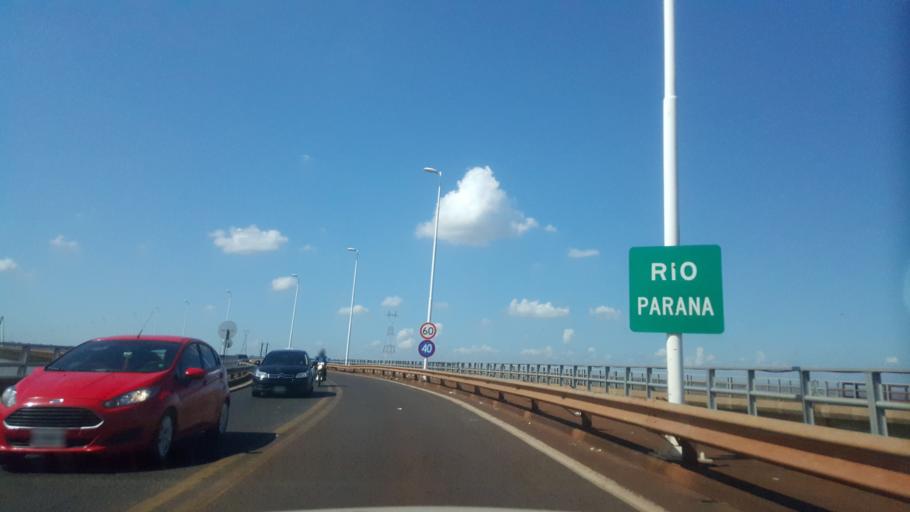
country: AR
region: Misiones
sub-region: Departamento de Capital
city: Posadas
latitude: -27.3762
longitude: -55.8805
